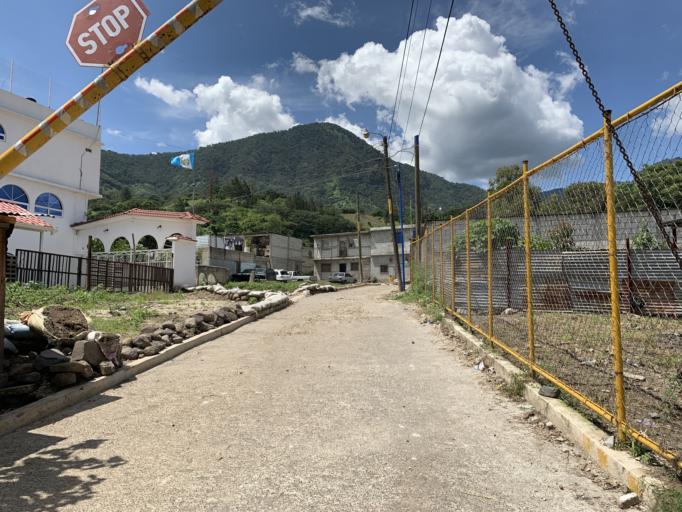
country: GT
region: Guatemala
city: Amatitlan
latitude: 14.4900
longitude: -90.6432
